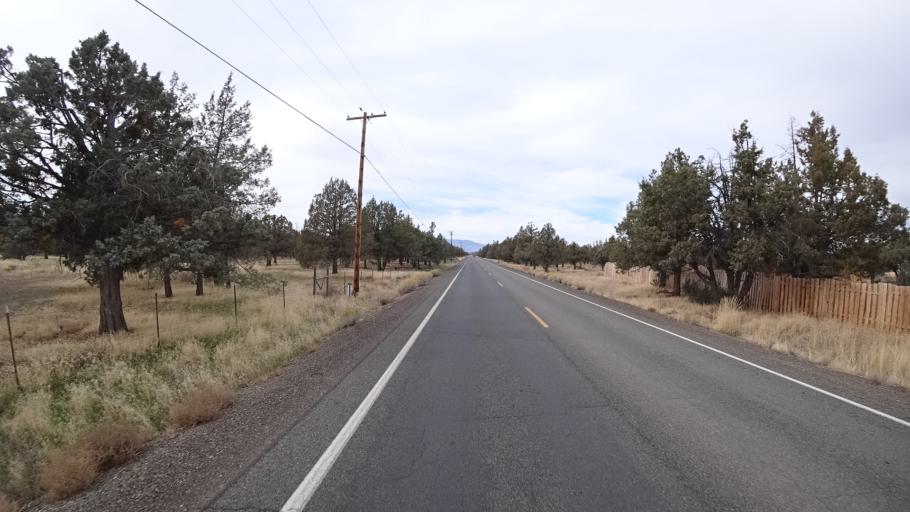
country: US
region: California
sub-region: Siskiyou County
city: Weed
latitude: 41.5934
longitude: -122.3144
